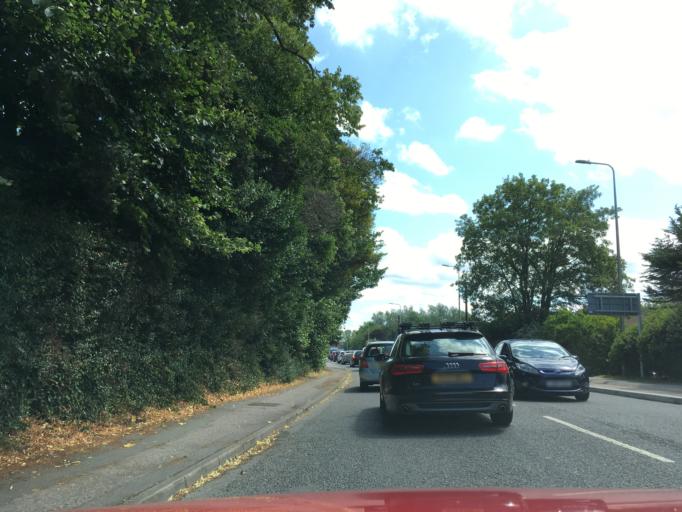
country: GB
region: England
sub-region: West Berkshire
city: Newbury
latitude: 51.4051
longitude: -1.3124
